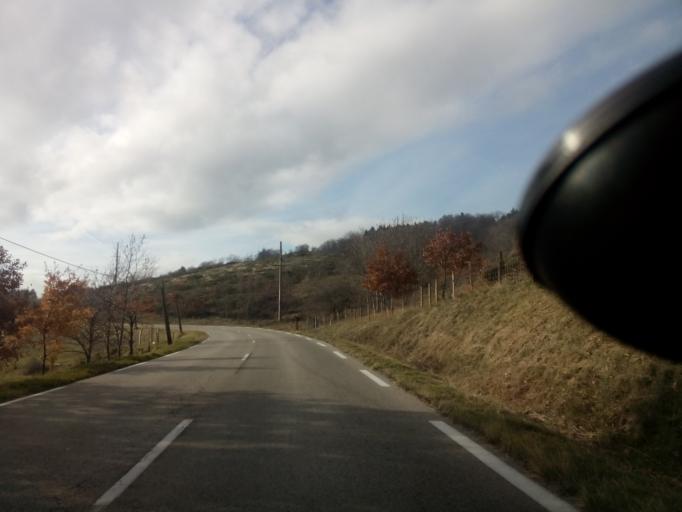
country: FR
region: Rhone-Alpes
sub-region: Departement de la Loire
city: Saint-Julien-Molin-Molette
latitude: 45.3353
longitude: 4.6441
